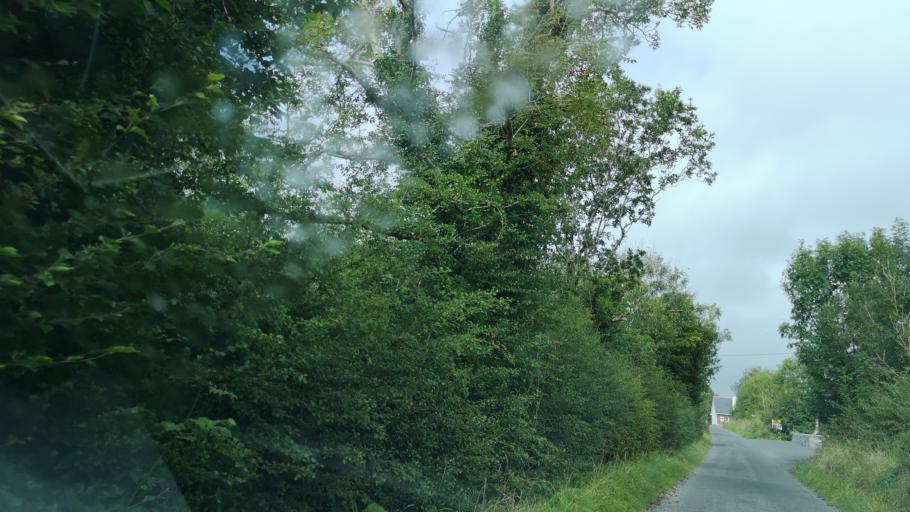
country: IE
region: Connaught
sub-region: County Galway
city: Loughrea
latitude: 53.3044
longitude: -8.6044
